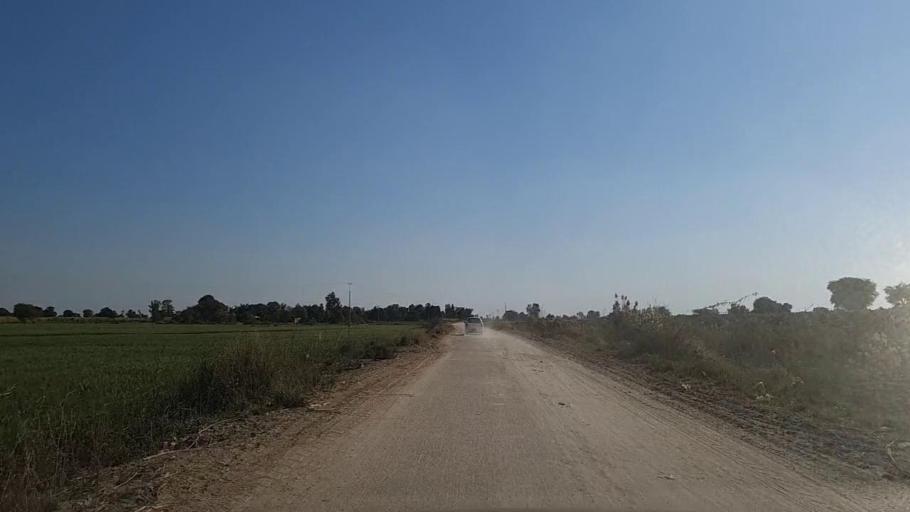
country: PK
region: Sindh
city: Nawabshah
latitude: 26.2343
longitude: 68.4259
